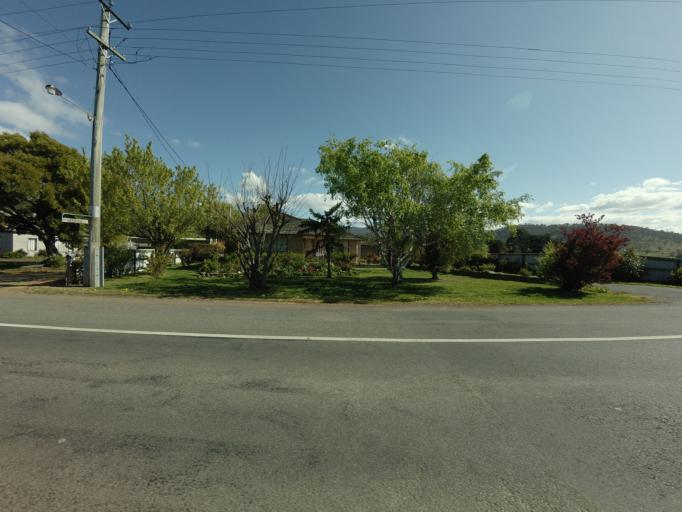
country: AU
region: Tasmania
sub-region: Derwent Valley
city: New Norfolk
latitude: -42.7731
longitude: 147.0342
